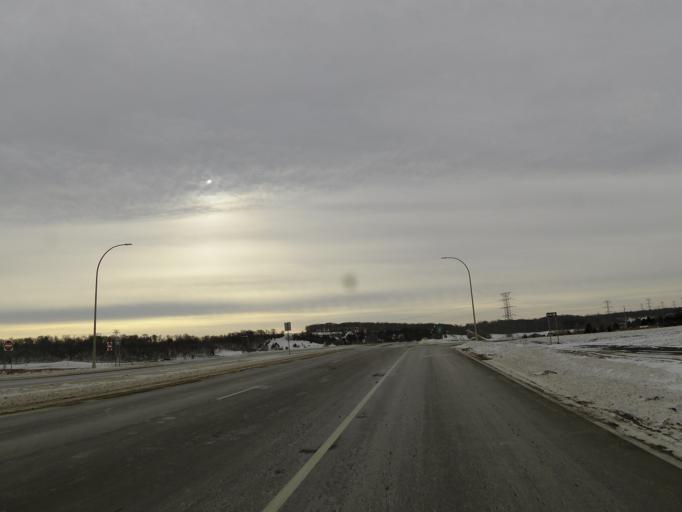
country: US
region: Minnesota
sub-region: Scott County
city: Shakopee
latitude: 44.7799
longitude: -93.5599
